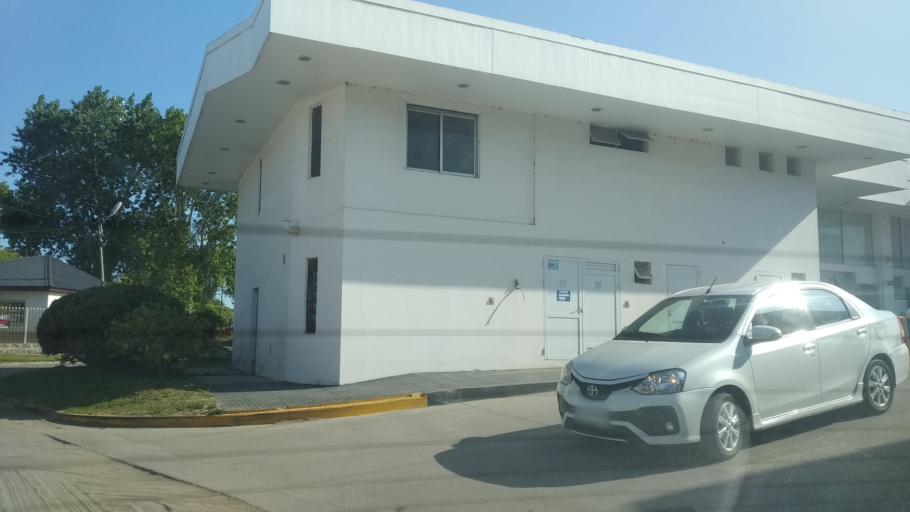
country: AR
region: Buenos Aires
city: Mar del Tuyu
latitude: -36.5328
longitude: -56.7143
